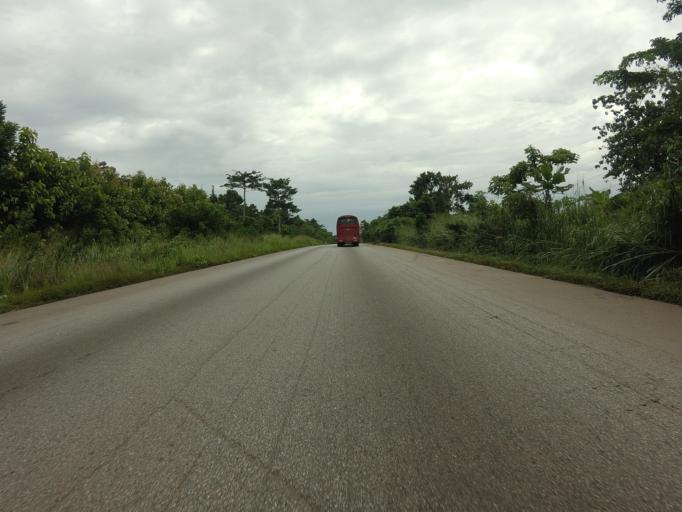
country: GH
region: Eastern
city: Nkawkaw
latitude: 6.6025
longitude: -0.9590
